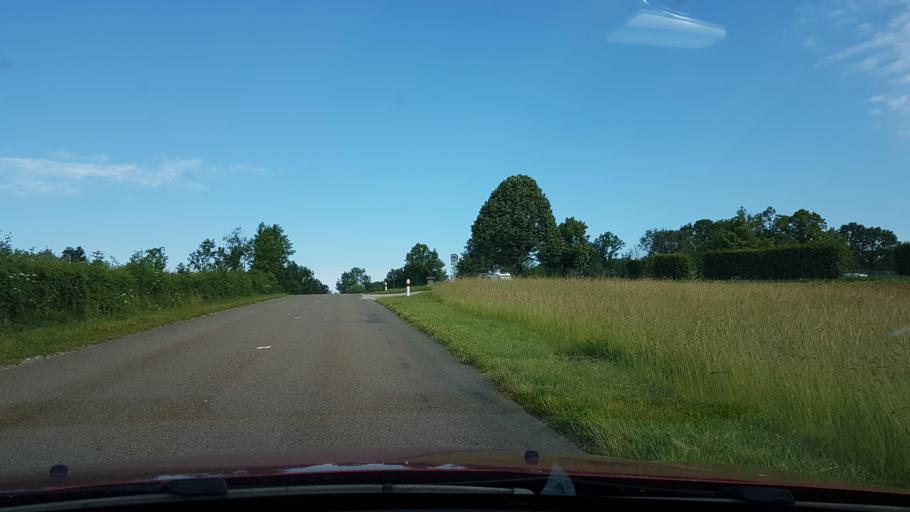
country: FR
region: Franche-Comte
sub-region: Departement du Jura
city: Clairvaux-les-Lacs
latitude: 46.5747
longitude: 5.7407
